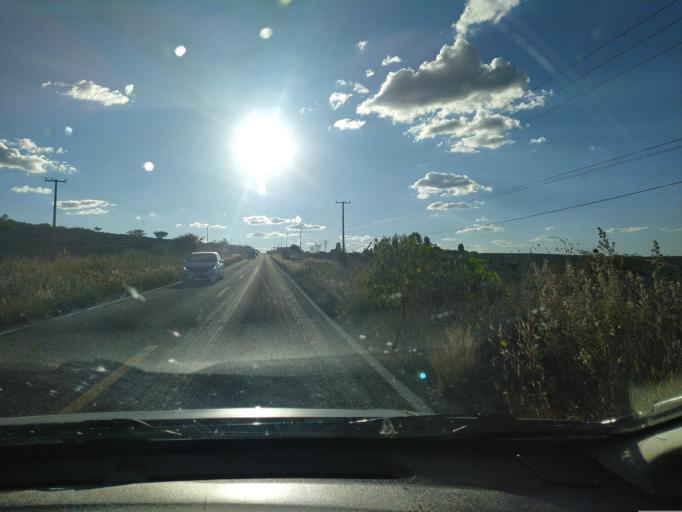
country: MX
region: Guanajuato
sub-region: Purisima del Rincon
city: Monte Grande
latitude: 21.0319
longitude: -101.9214
